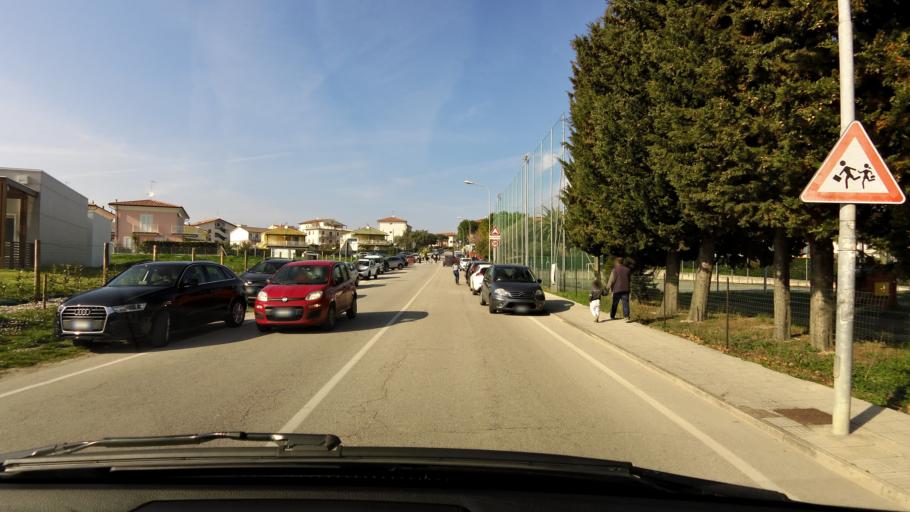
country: IT
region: The Marches
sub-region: Provincia di Ancona
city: Marcelli
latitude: 43.4940
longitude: 13.6228
